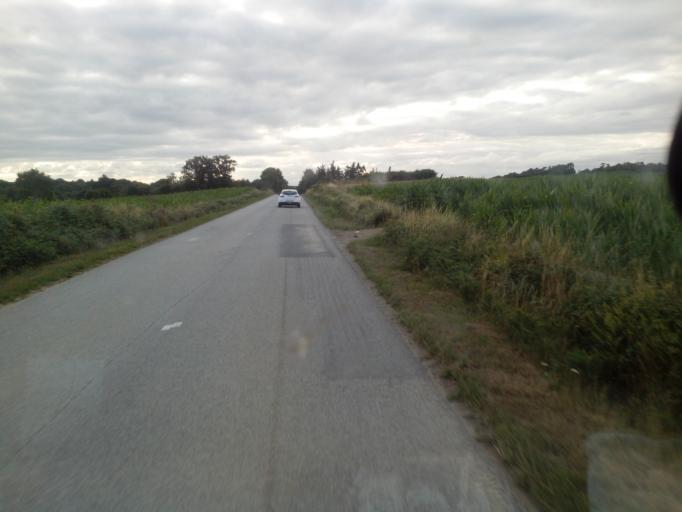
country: FR
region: Brittany
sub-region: Departement du Morbihan
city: Mauron
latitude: 48.0661
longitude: -2.2218
